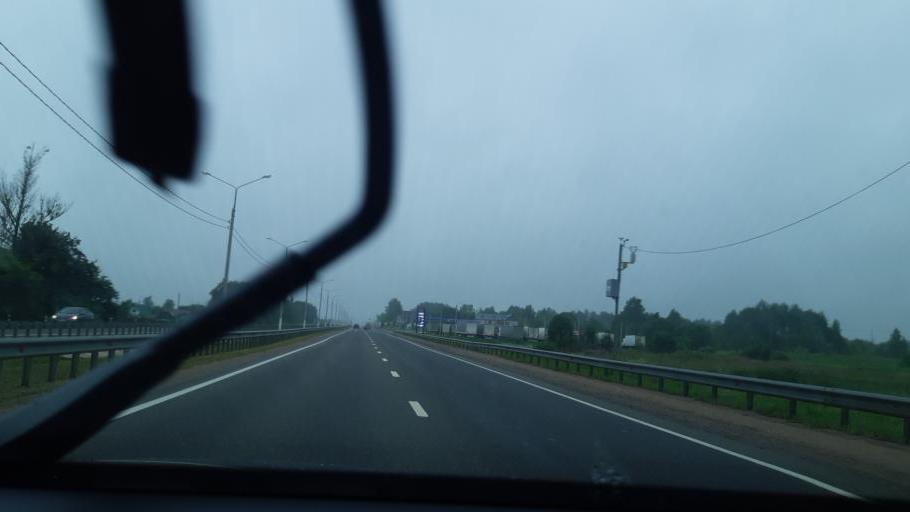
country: RU
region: Smolensk
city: Talashkino
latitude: 54.6455
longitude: 32.1726
